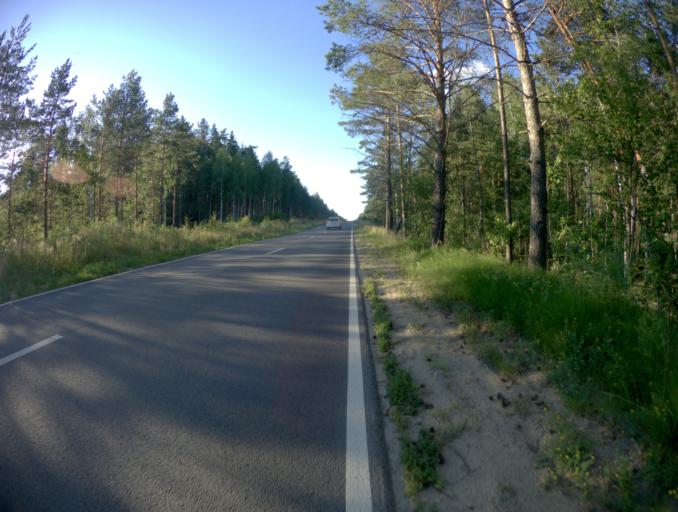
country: RU
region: Vladimir
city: Galitsy
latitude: 56.0376
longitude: 42.8625
